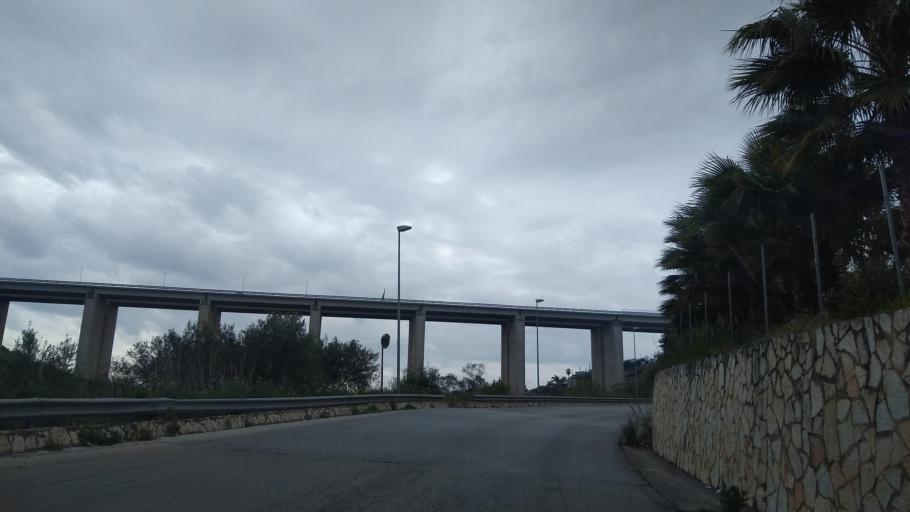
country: IT
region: Sicily
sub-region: Trapani
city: Alcamo
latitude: 38.0166
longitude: 12.9521
